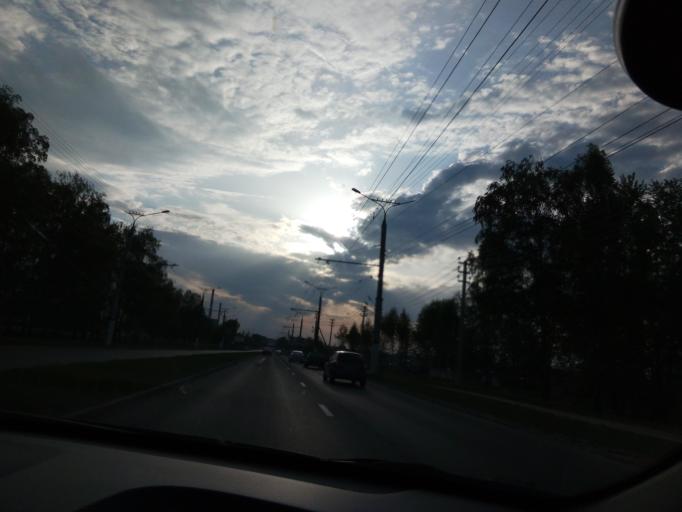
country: RU
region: Chuvashia
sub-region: Cheboksarskiy Rayon
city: Cheboksary
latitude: 56.1267
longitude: 47.3415
